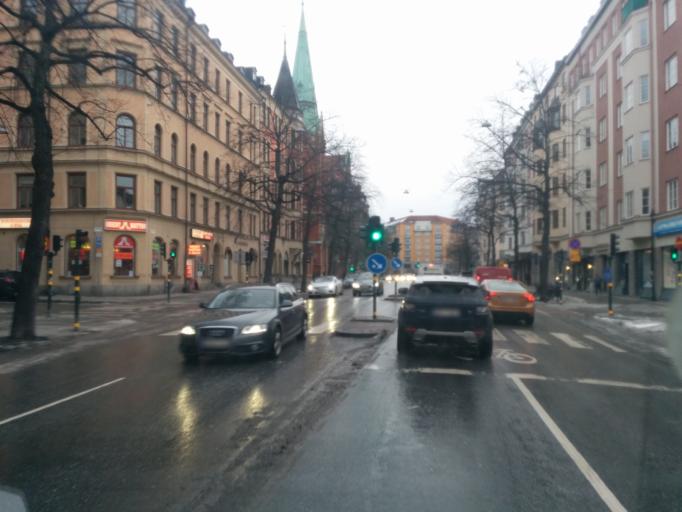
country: SE
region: Stockholm
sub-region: Stockholms Kommun
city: Stockholm
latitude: 59.3467
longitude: 18.0616
